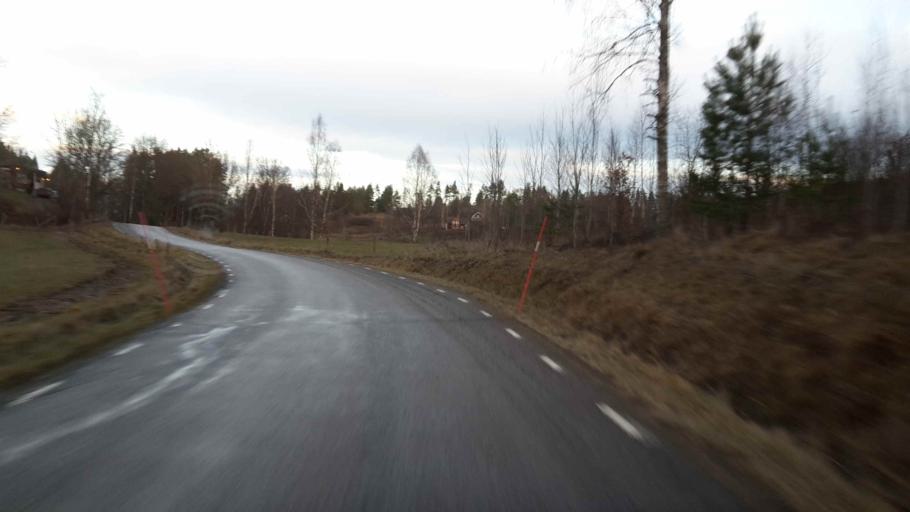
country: SE
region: OEstergoetland
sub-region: Valdemarsviks Kommun
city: Gusum
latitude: 58.1644
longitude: 16.3330
